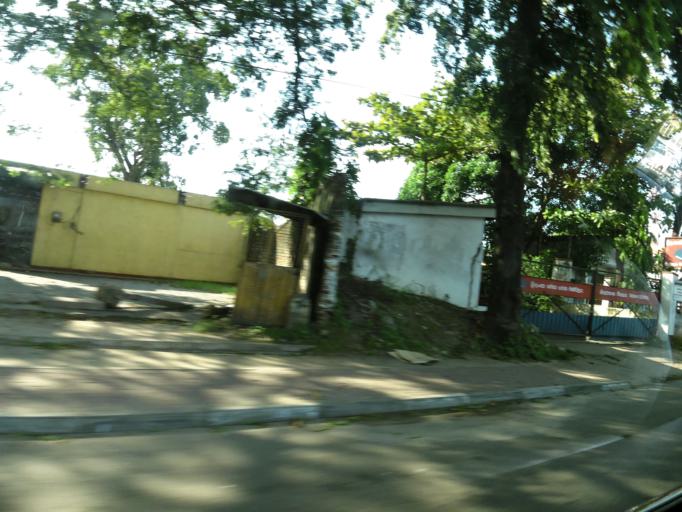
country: LK
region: Western
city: Kolonnawa
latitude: 6.9445
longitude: 79.8782
